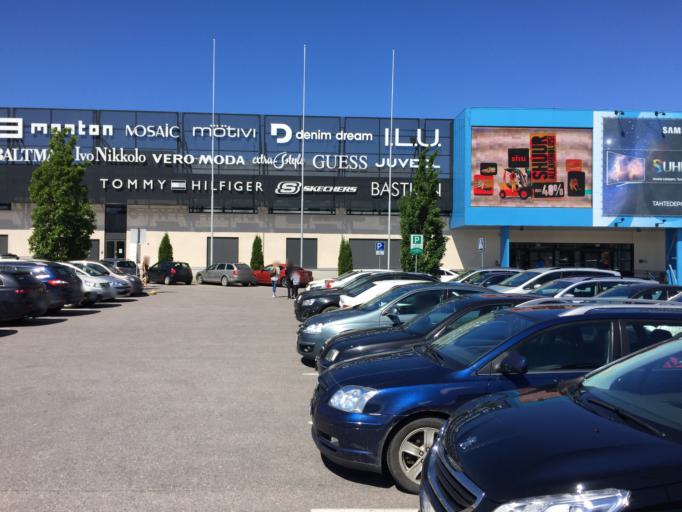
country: EE
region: Harju
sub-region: Saue vald
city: Laagri
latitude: 59.4259
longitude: 24.6522
